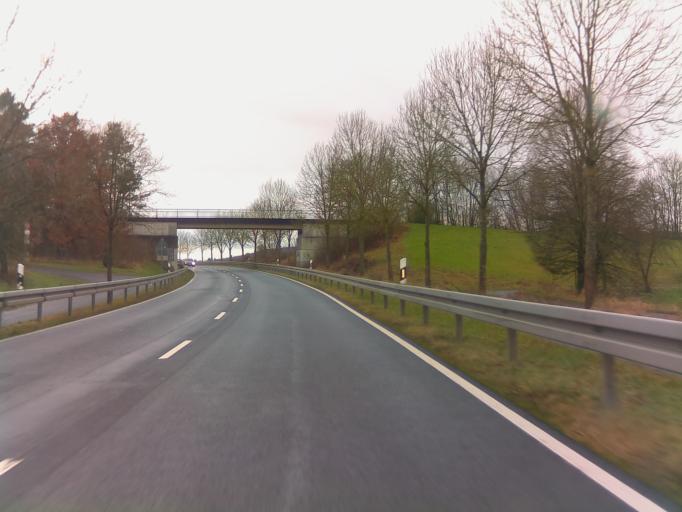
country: DE
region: Hesse
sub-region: Regierungsbezirk Darmstadt
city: Bad Soden-Salmunster
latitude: 50.3007
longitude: 9.4094
